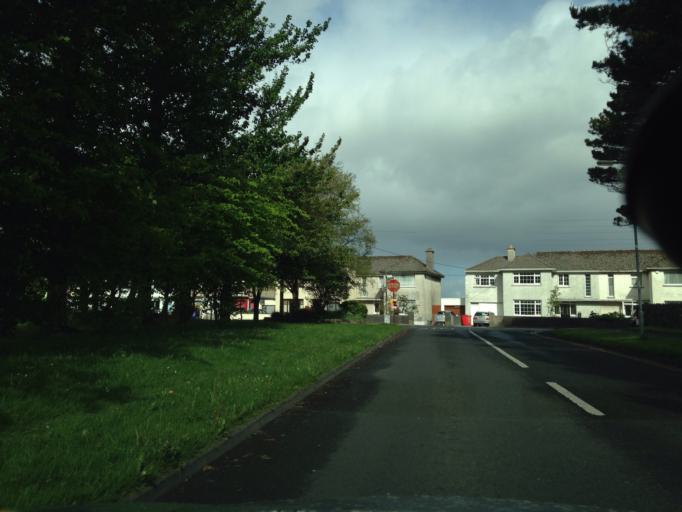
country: IE
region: Connaught
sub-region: County Galway
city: Gaillimh
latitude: 53.2773
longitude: -9.0223
